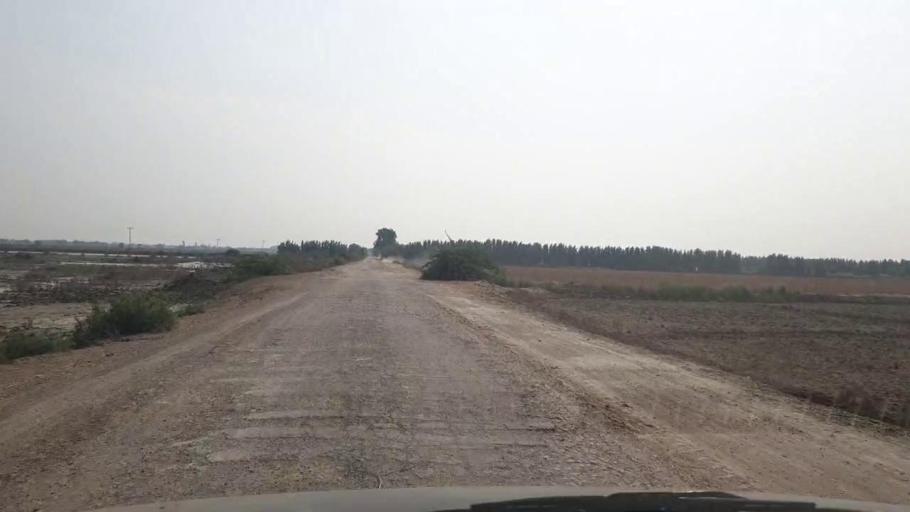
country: PK
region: Sindh
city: Tando Muhammad Khan
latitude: 25.0448
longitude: 68.3902
